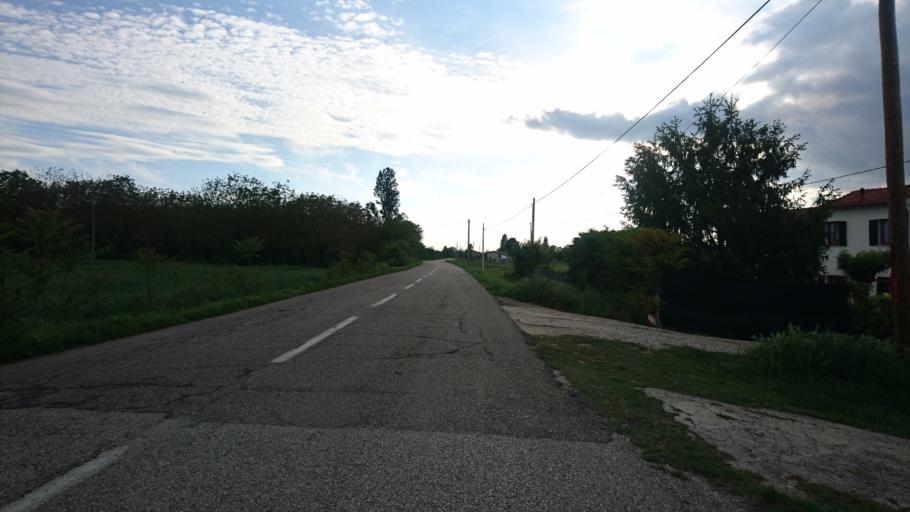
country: IT
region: Veneto
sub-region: Provincia di Rovigo
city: Ceneselli
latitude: 45.0035
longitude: 11.3955
